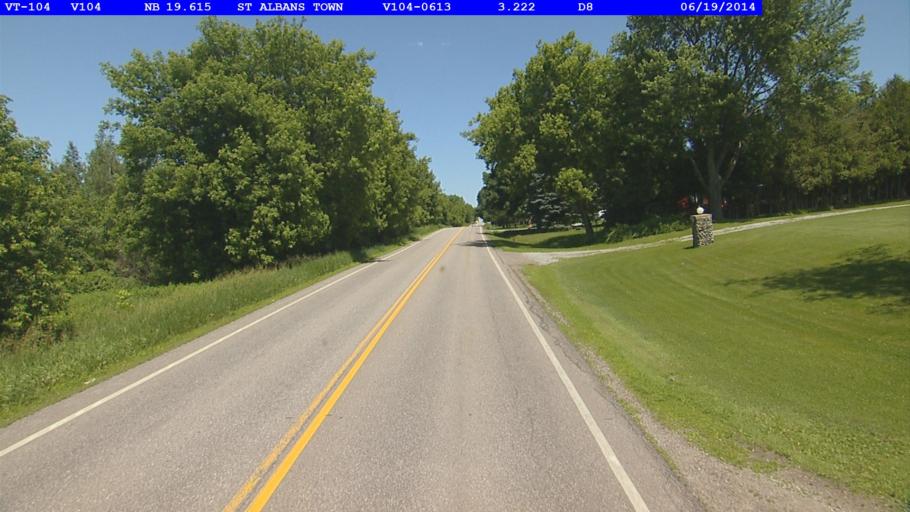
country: US
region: Vermont
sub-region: Franklin County
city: Saint Albans
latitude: 44.8171
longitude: -73.0598
